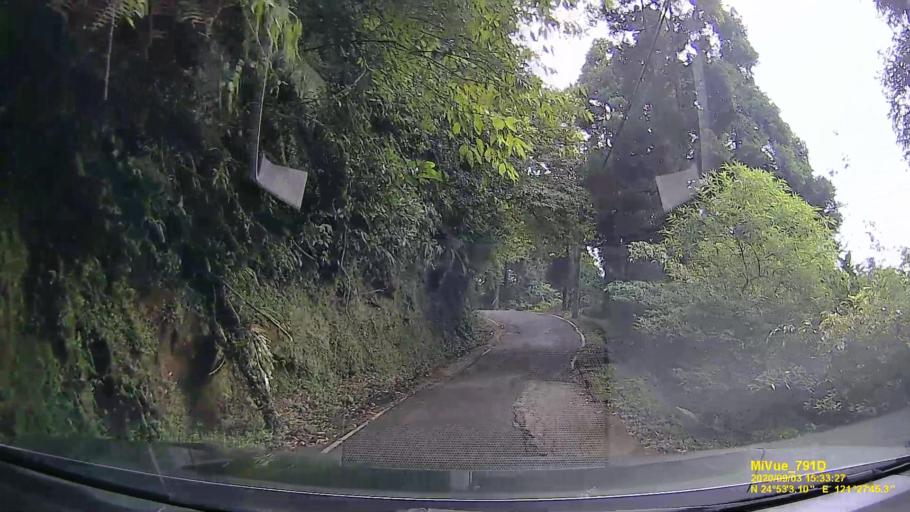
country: TW
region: Taipei
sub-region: Taipei
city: Banqiao
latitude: 24.8841
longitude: 121.4625
